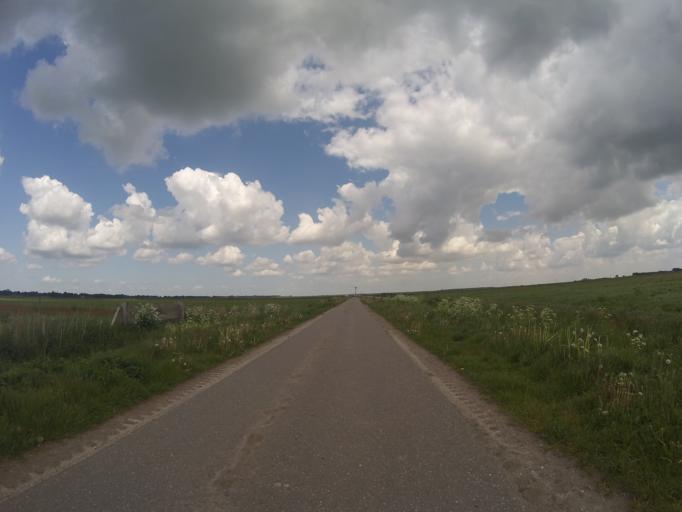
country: NL
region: Utrecht
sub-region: Gemeente Baarn
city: Baarn
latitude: 52.2462
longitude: 5.2869
